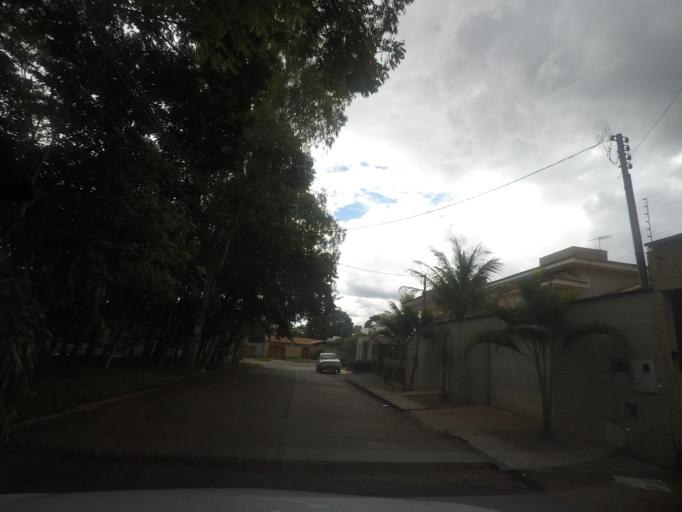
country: BR
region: Goias
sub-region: Goiania
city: Goiania
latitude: -16.6437
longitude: -49.2261
